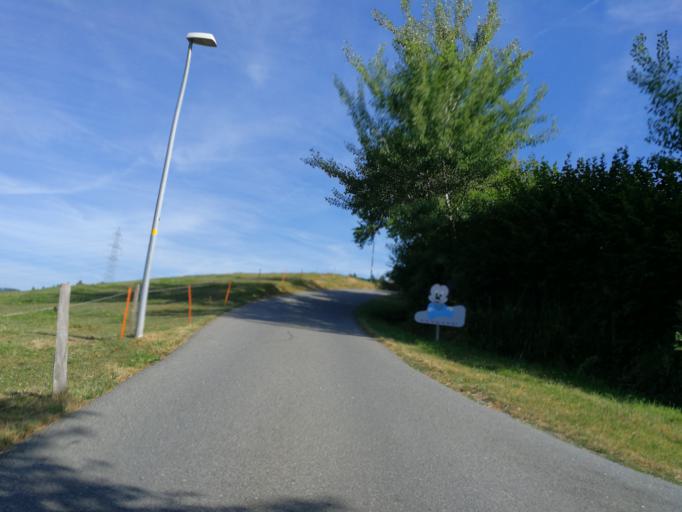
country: CH
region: Saint Gallen
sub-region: Wahlkreis See-Gaster
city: Gommiswald
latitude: 47.2379
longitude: 9.0052
